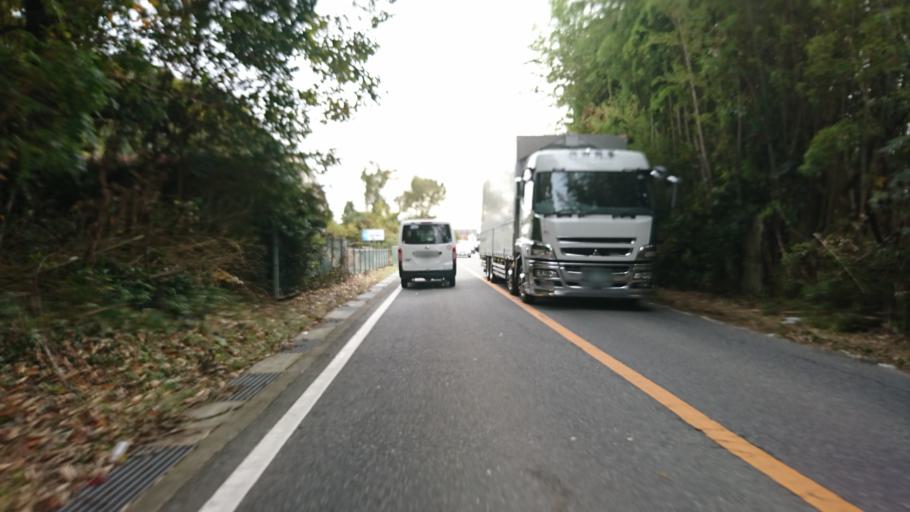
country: JP
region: Hyogo
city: Ono
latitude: 34.8019
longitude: 134.9252
